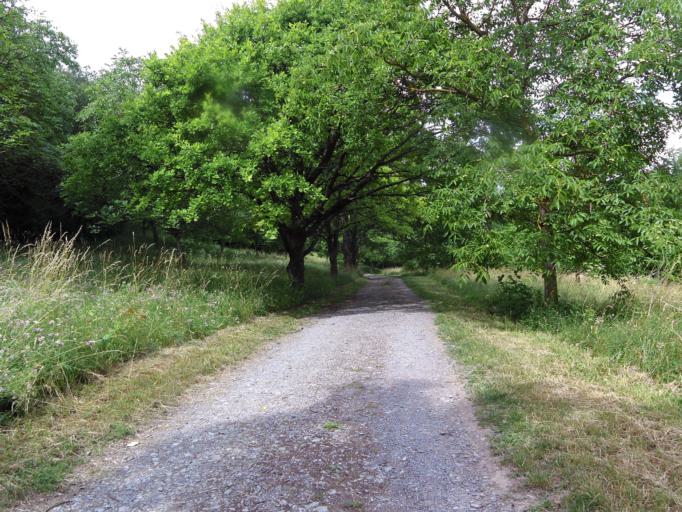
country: DE
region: Bavaria
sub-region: Regierungsbezirk Unterfranken
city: Wuerzburg
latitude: 49.7937
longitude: 9.9694
